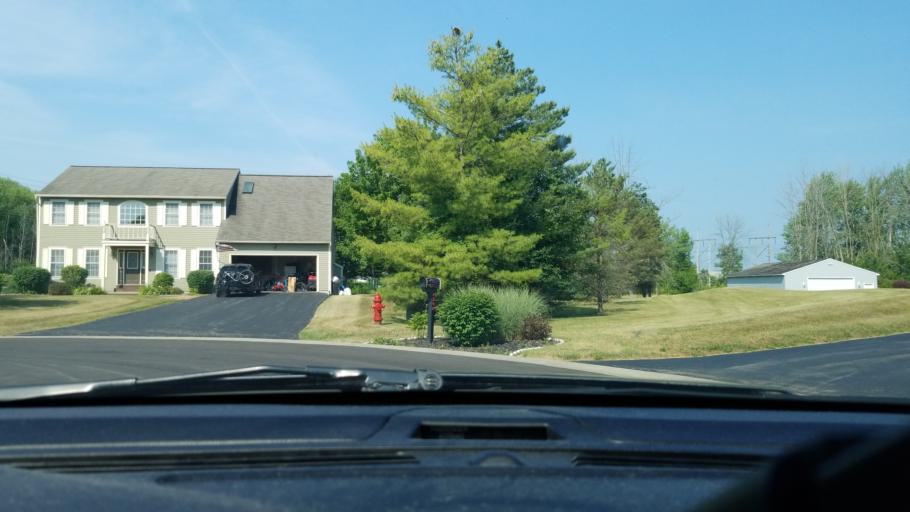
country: US
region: New York
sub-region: Onondaga County
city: East Syracuse
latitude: 43.0981
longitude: -76.0728
